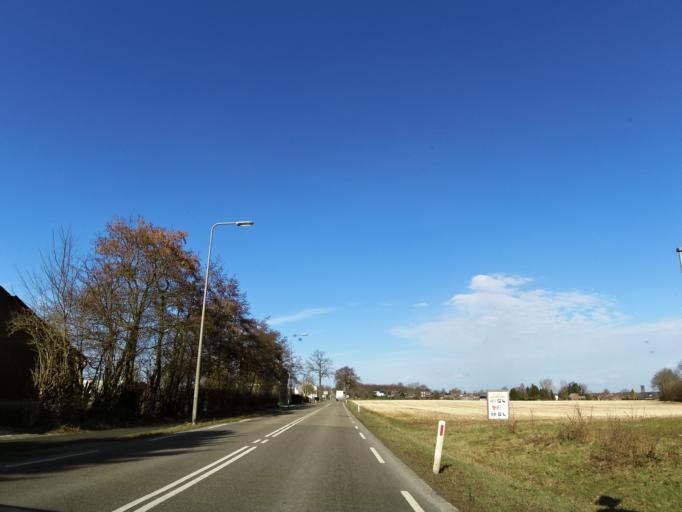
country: NL
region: Limburg
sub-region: Eijsden-Margraten
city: Margraten
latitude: 50.7956
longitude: 5.8326
